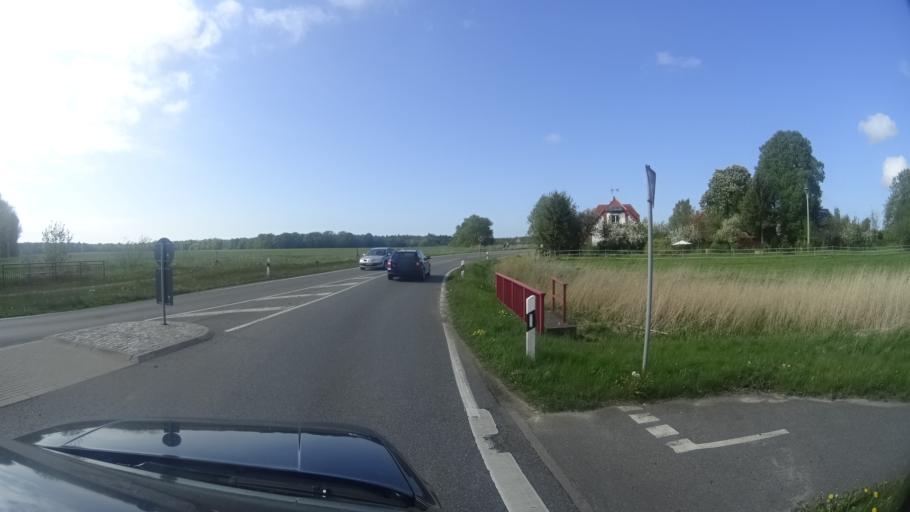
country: DE
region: Mecklenburg-Vorpommern
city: Monchhagen
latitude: 54.1782
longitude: 12.2057
